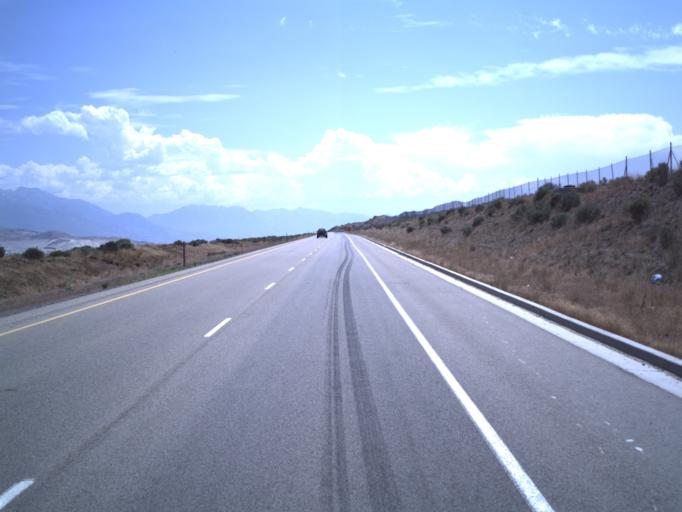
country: US
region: Utah
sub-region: Salt Lake County
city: Bluffdale
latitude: 40.4799
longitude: -111.9863
